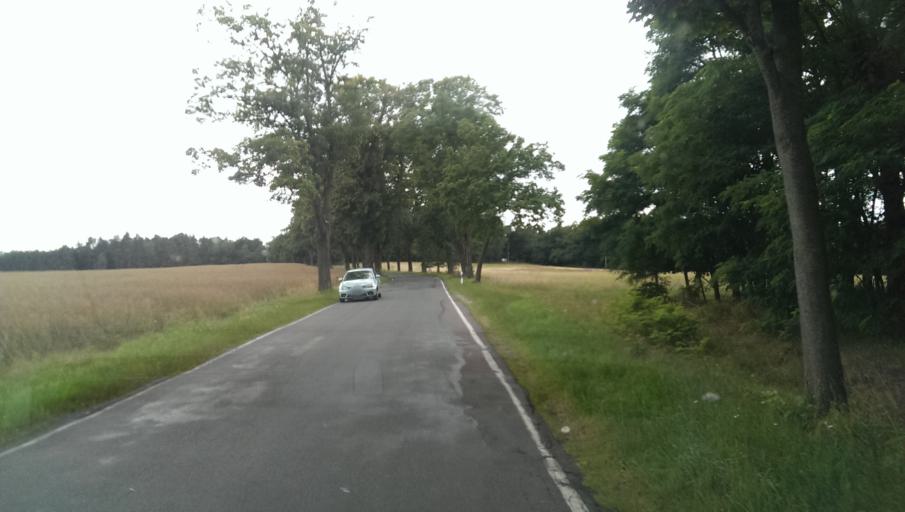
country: DE
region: Saxony-Anhalt
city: Nudersdorf
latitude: 51.9117
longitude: 12.5225
